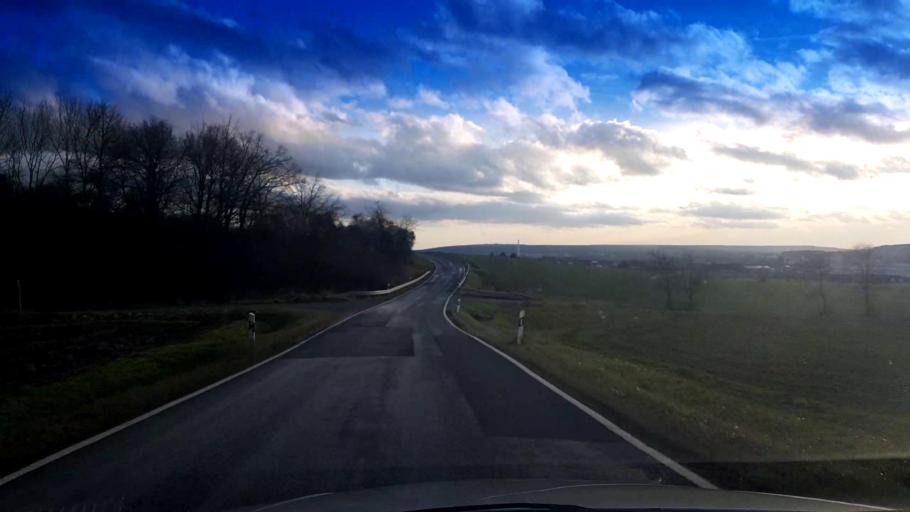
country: DE
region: Bavaria
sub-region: Upper Franconia
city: Buttenheim
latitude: 49.8145
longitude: 11.0267
